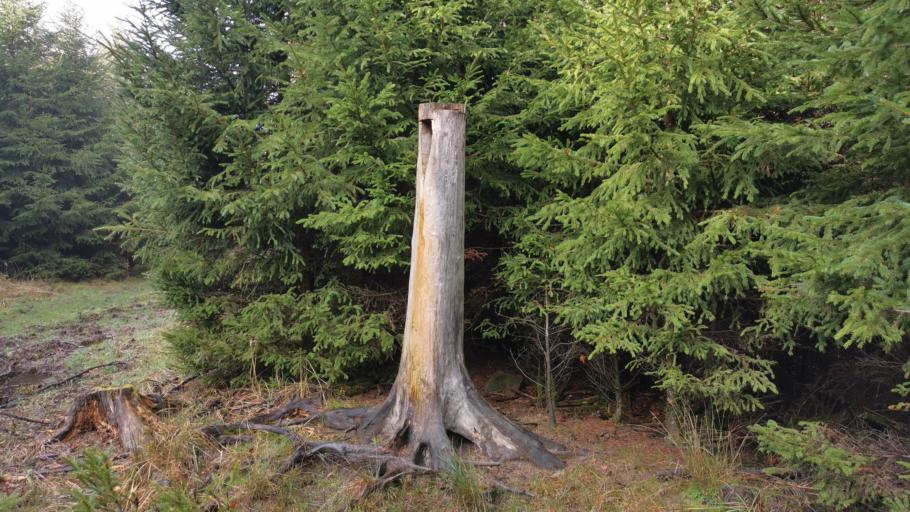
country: DE
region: Bavaria
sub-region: Upper Bavaria
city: Baierbrunn
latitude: 48.0251
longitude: 11.4677
